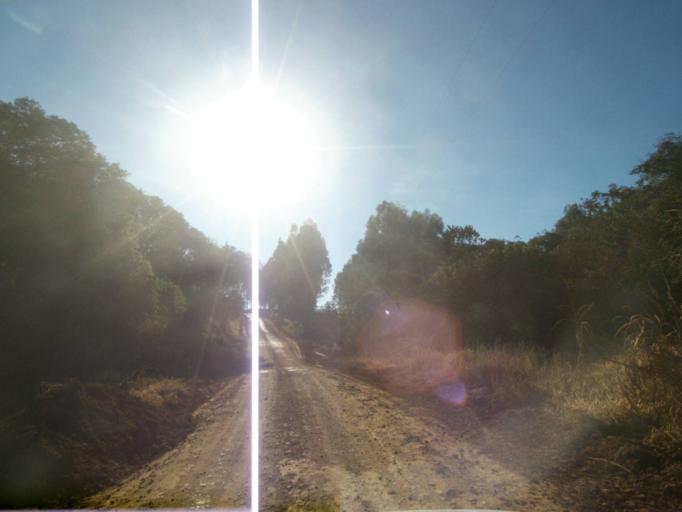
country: BR
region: Parana
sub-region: Tibagi
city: Tibagi
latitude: -24.5271
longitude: -50.4920
